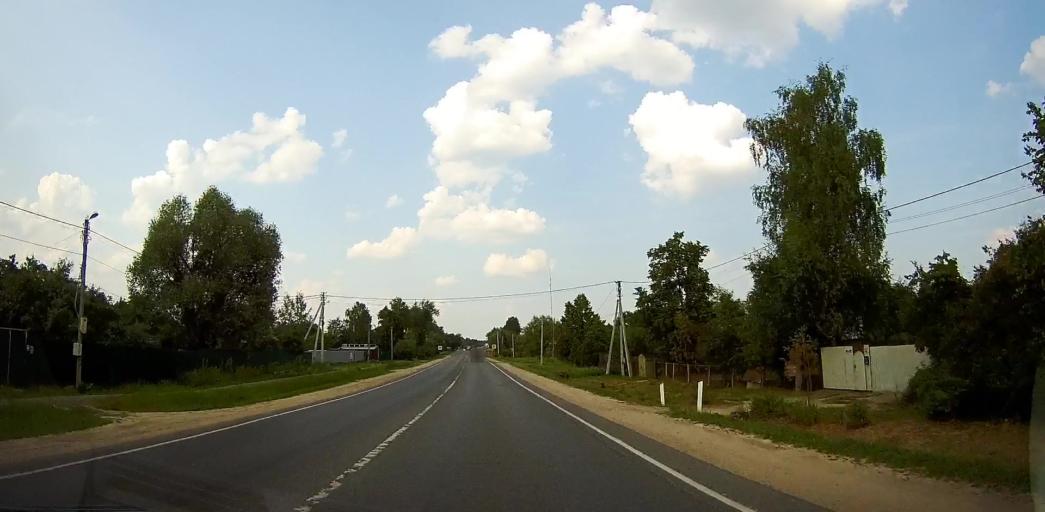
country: RU
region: Moskovskaya
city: Mikhnevo
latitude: 55.1325
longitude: 37.9491
